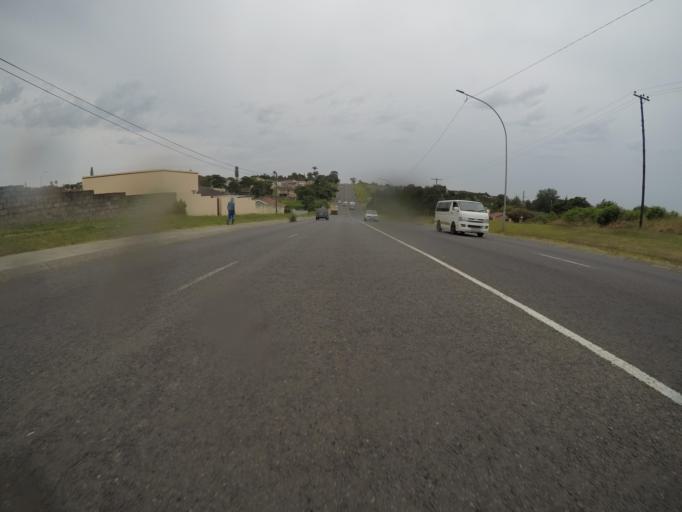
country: ZA
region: Eastern Cape
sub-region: Buffalo City Metropolitan Municipality
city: East London
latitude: -32.9970
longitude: 27.8478
